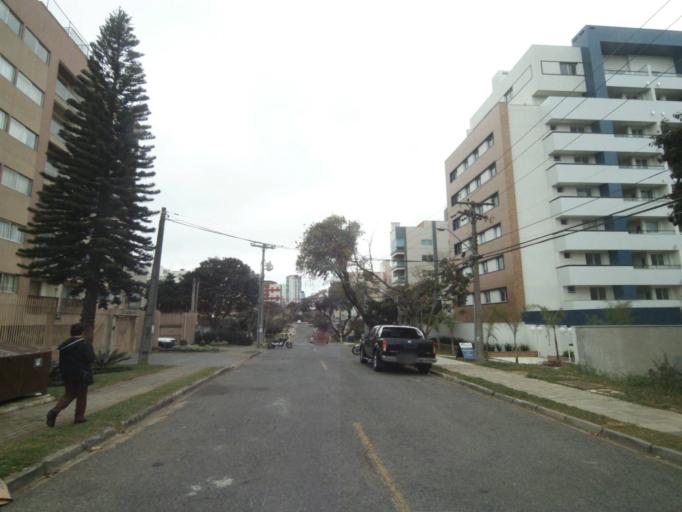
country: BR
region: Parana
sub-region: Curitiba
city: Curitiba
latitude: -25.4563
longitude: -49.2966
